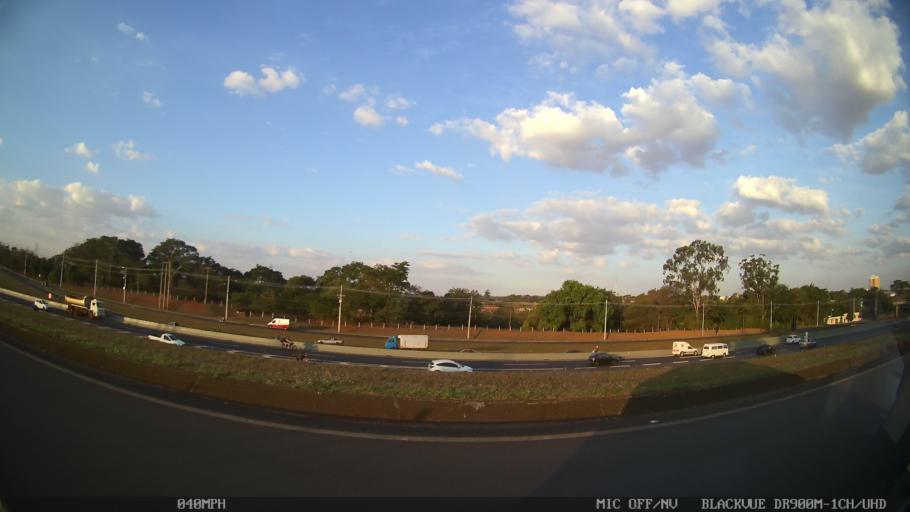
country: BR
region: Sao Paulo
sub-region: Ribeirao Preto
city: Ribeirao Preto
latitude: -21.1522
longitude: -47.7579
